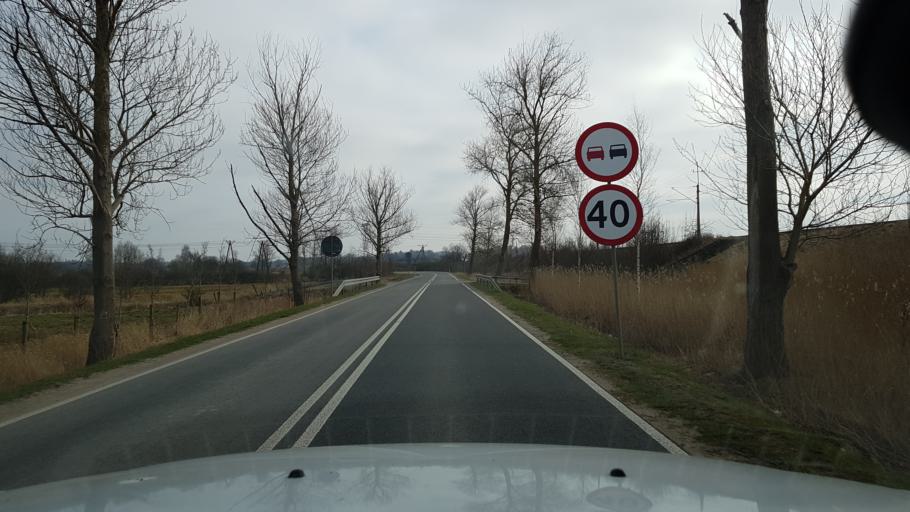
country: PL
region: West Pomeranian Voivodeship
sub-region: Powiat koszalinski
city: Sianow
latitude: 54.2340
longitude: 16.2700
